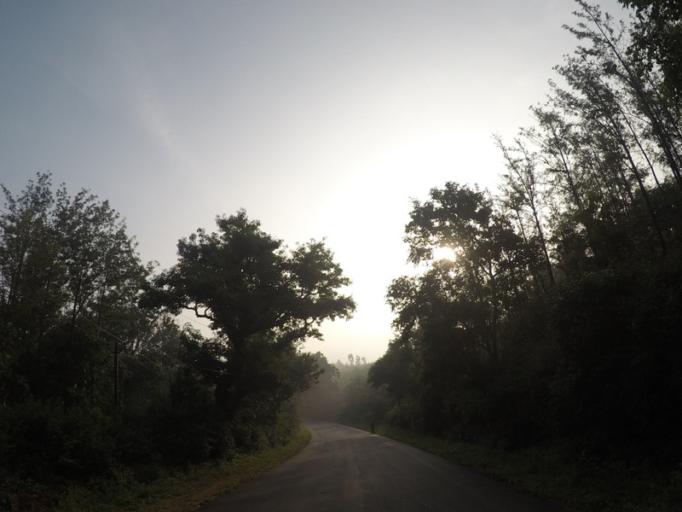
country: IN
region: Karnataka
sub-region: Chikmagalur
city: Chikmagalur
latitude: 13.3978
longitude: 75.7831
